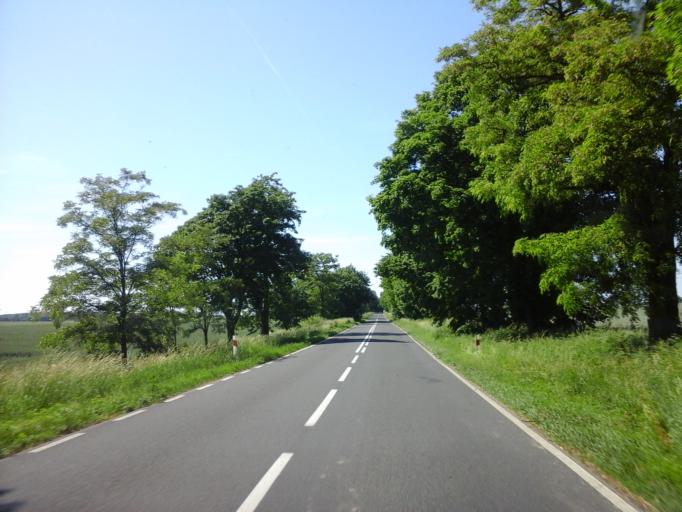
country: PL
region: West Pomeranian Voivodeship
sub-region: Powiat choszczenski
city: Krzecin
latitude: 53.1312
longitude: 15.5333
